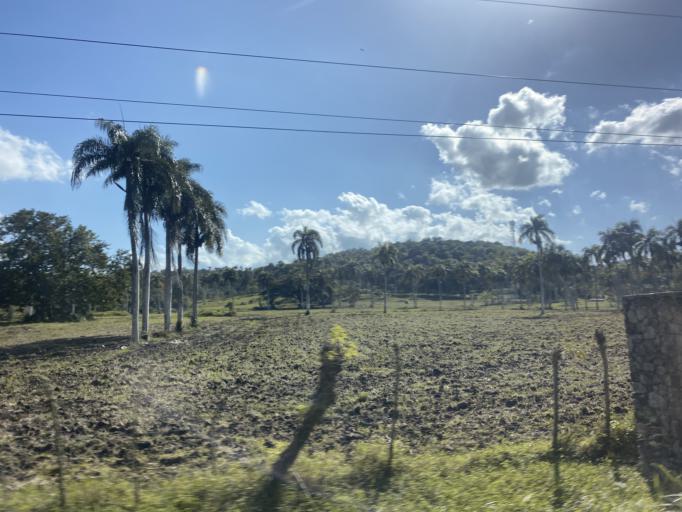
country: DO
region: Espaillat
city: Gaspar Hernandez
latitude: 19.6395
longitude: -70.2524
